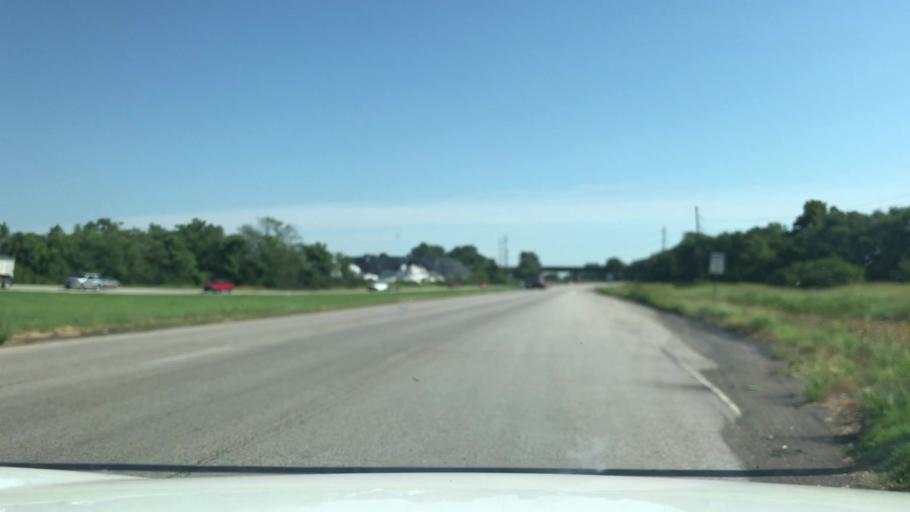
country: US
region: Illinois
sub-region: Madison County
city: Venice
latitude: 38.6721
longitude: -90.1756
